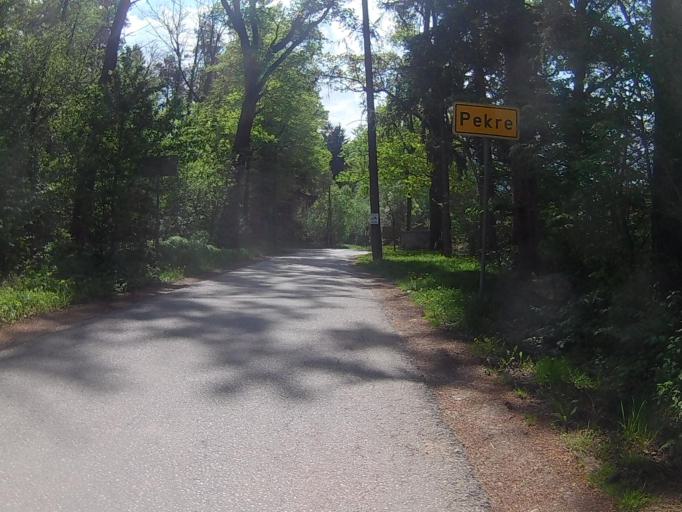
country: SI
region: Maribor
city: Pekre
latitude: 46.5480
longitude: 15.6037
